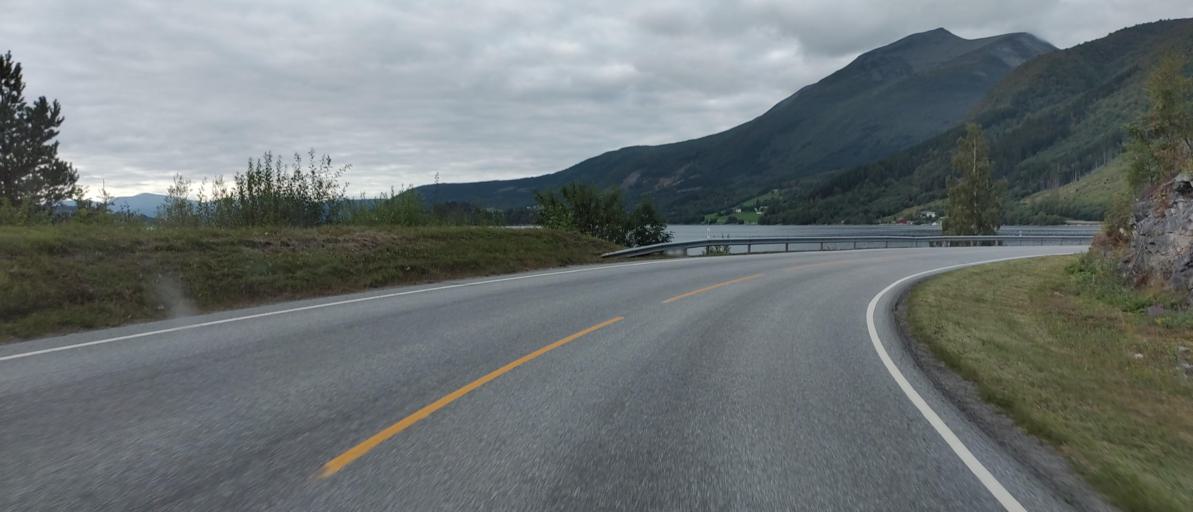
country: NO
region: More og Romsdal
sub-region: Rauma
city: Andalsnes
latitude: 62.5871
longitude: 7.5369
